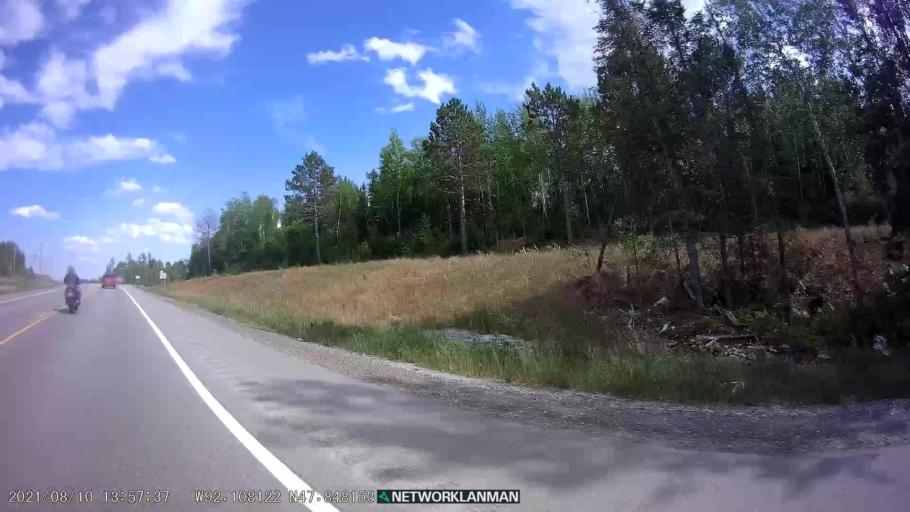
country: US
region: Minnesota
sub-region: Saint Louis County
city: Babbitt
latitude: 47.8481
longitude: -92.1077
